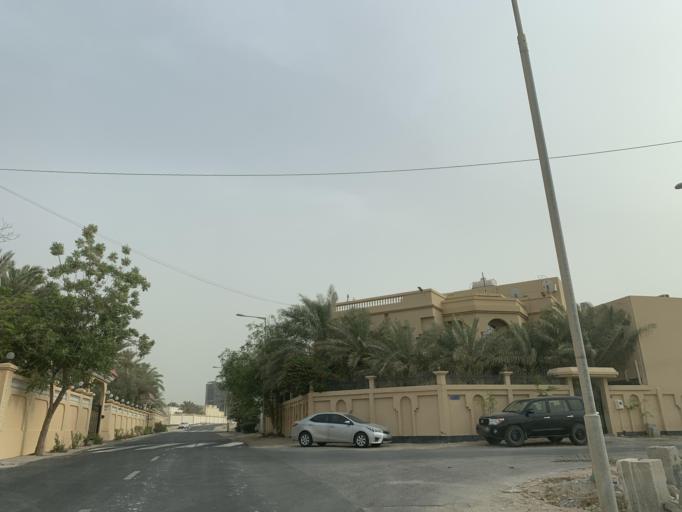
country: BH
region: Northern
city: Ar Rifa'
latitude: 26.1397
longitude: 50.5274
